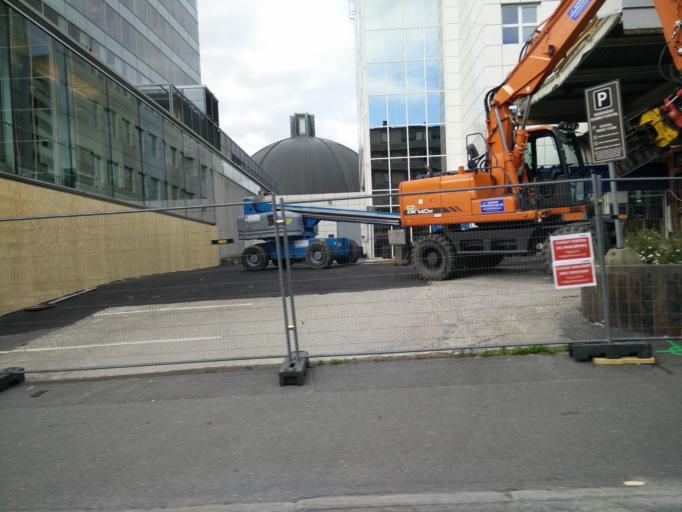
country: NO
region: Oslo
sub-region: Oslo
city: Sjolyststranda
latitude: 59.9306
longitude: 10.7120
